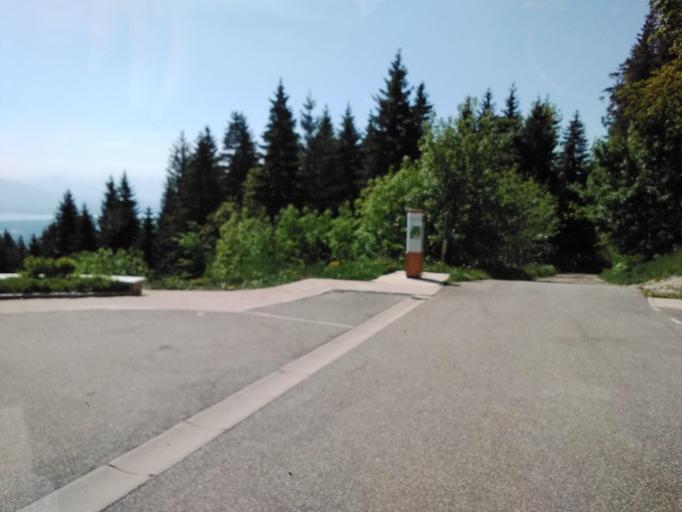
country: FR
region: Rhone-Alpes
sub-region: Departement de l'Ain
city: Gex
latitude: 46.3589
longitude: 6.0259
